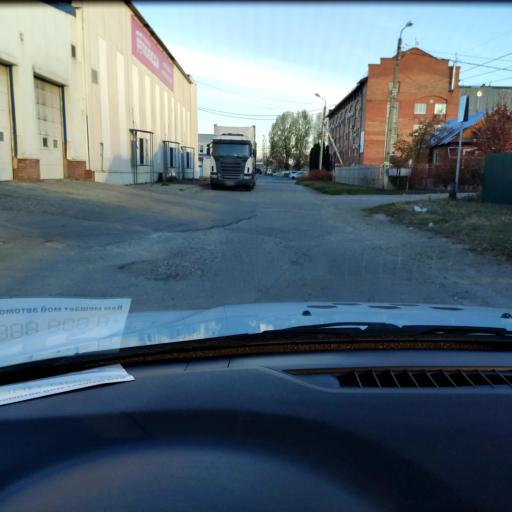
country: RU
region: Samara
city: Tol'yatti
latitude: 53.5389
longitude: 49.4131
